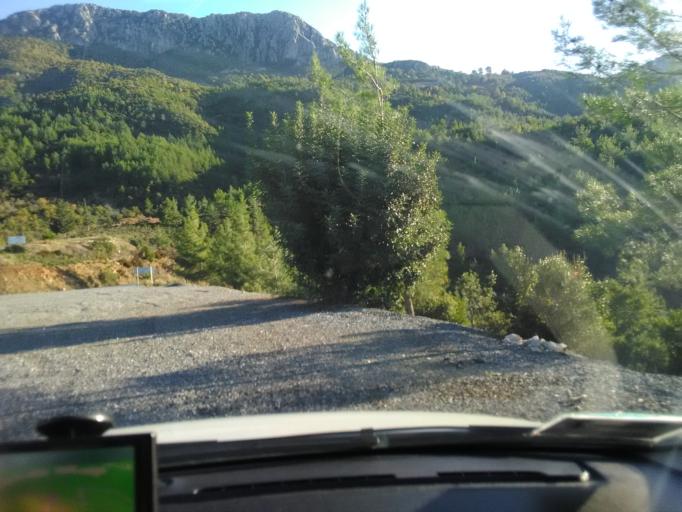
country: TR
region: Antalya
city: Gazipasa
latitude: 36.3063
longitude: 32.3983
